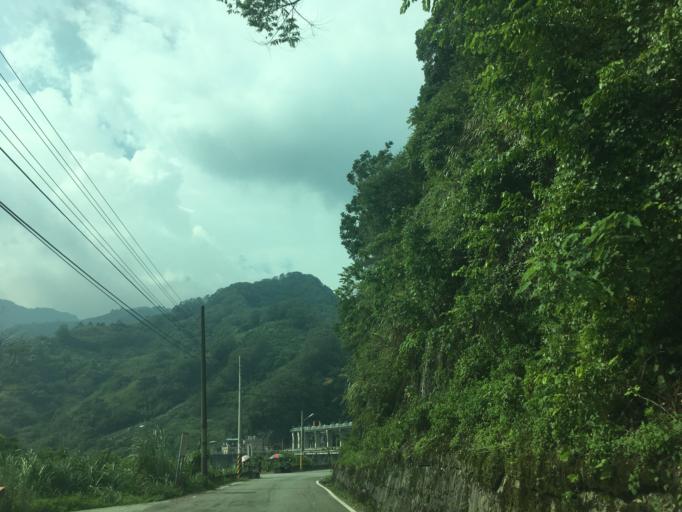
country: TW
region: Taiwan
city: Fengyuan
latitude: 24.3419
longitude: 120.9362
